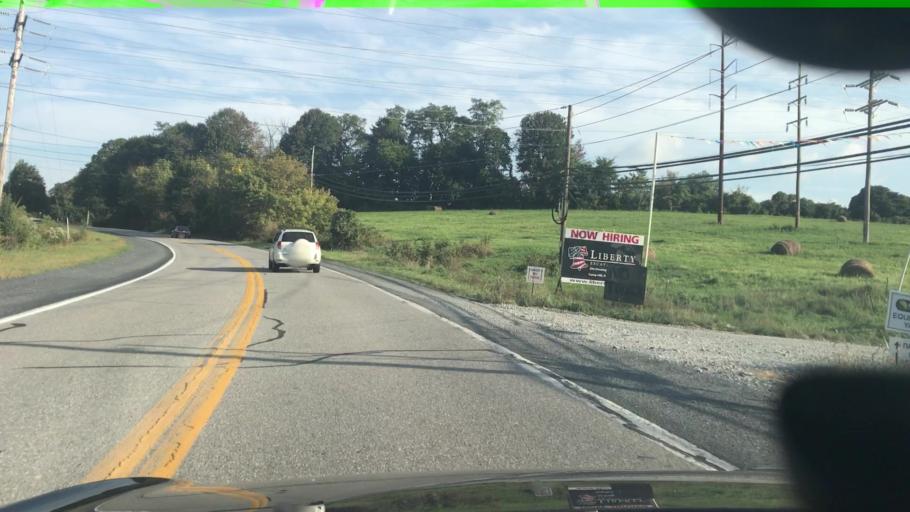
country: US
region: Pennsylvania
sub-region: Cumberland County
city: Shiremanstown
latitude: 40.2082
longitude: -76.9415
